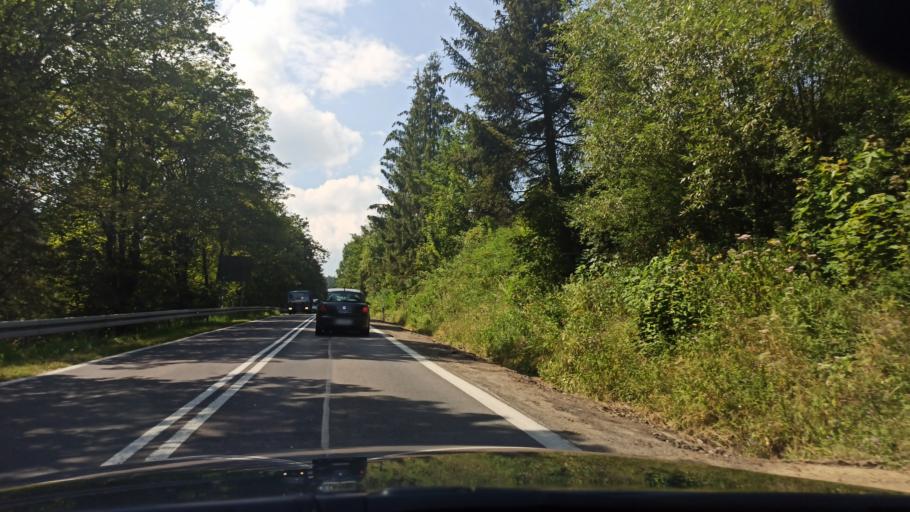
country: PL
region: Lesser Poland Voivodeship
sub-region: Powiat nowotarski
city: Krosnica
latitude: 49.4367
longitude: 20.3695
